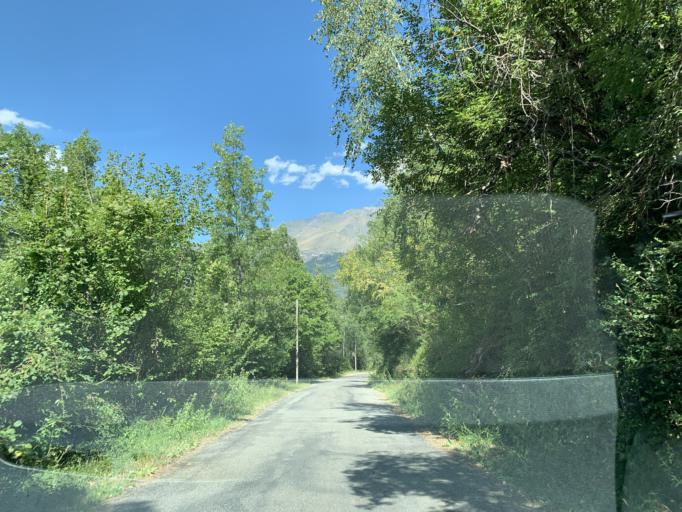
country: ES
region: Aragon
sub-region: Provincia de Huesca
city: Hoz de Jaca
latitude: 42.6948
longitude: -0.3094
